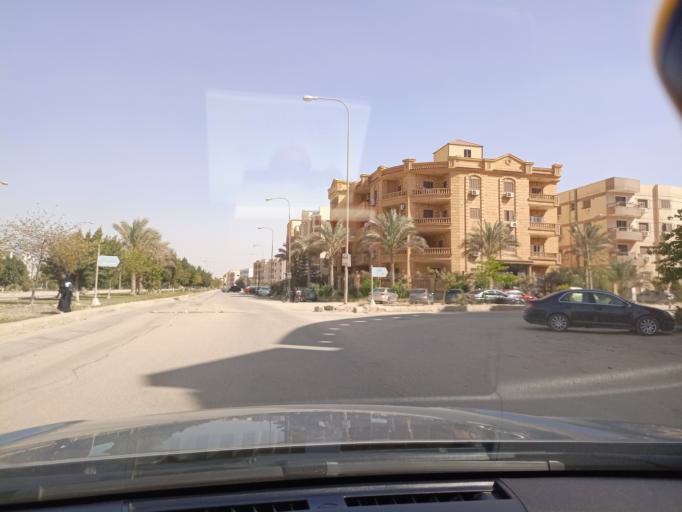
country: EG
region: Muhafazat al Qalyubiyah
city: Al Khankah
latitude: 30.2291
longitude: 31.4436
